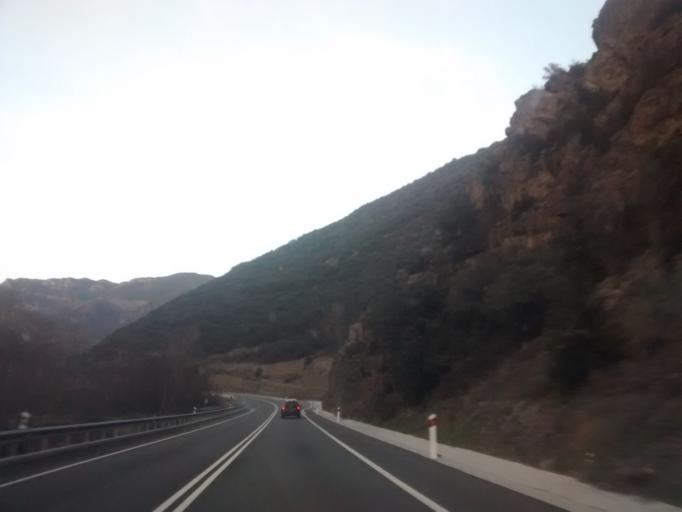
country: ES
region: Catalonia
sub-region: Provincia de Lleida
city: la Seu d'Urgell
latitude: 42.4086
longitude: 1.4691
